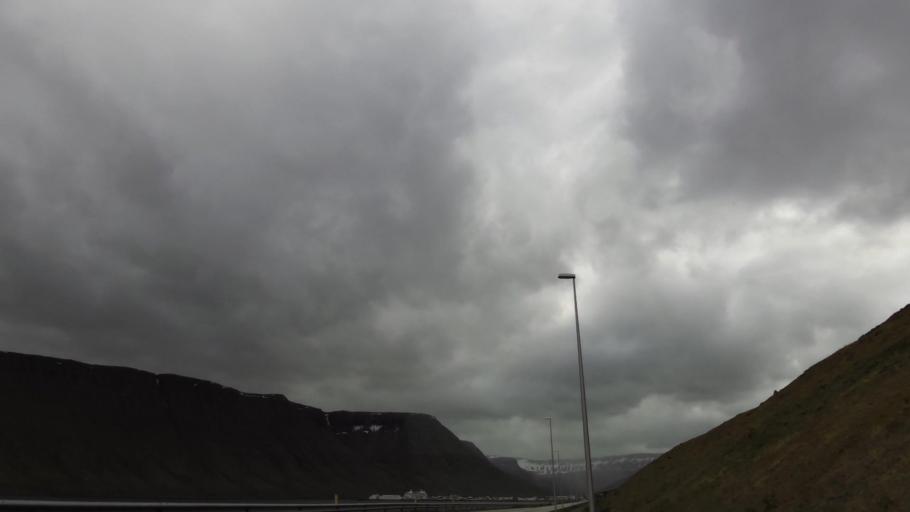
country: IS
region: Westfjords
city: Isafjoerdur
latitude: 66.0921
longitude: -23.1138
